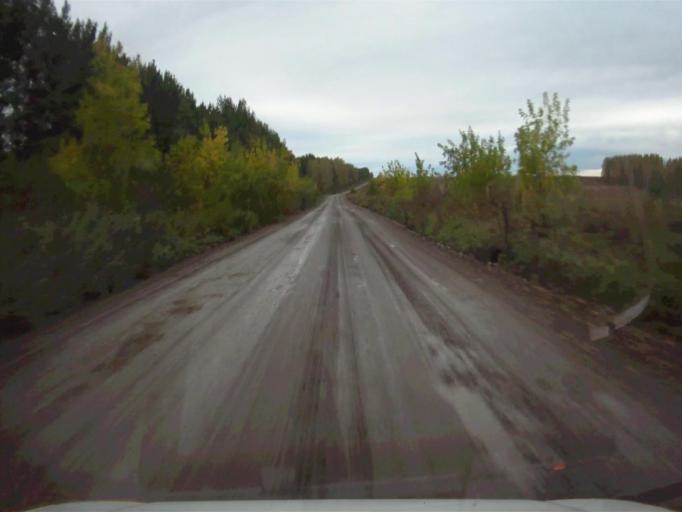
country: RU
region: Sverdlovsk
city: Mikhaylovsk
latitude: 56.1490
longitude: 59.2736
